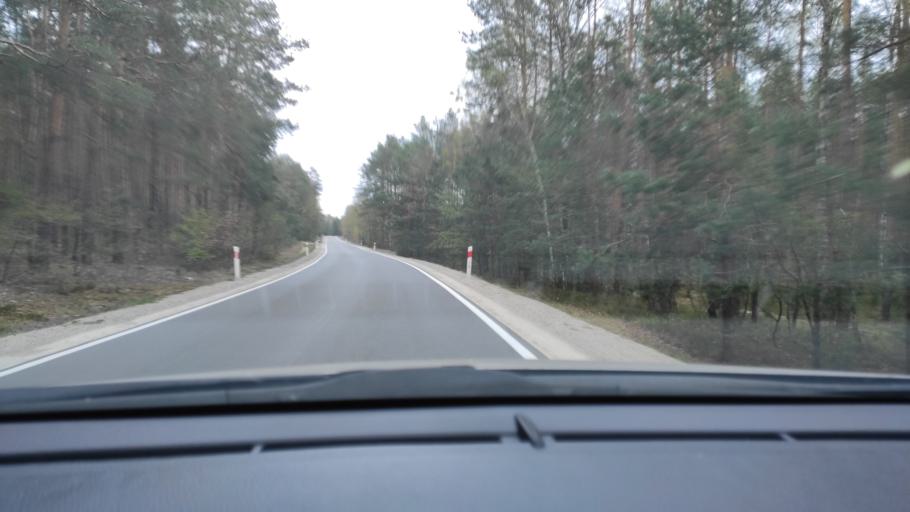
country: PL
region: Masovian Voivodeship
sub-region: Powiat zwolenski
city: Zwolen
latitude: 51.4087
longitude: 21.5202
